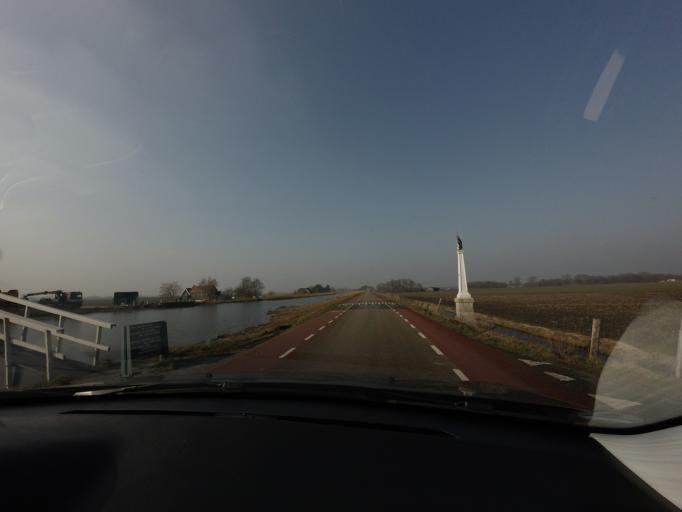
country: NL
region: North Holland
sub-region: Gemeente Opmeer
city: Opmeer
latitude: 52.6174
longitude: 4.9330
